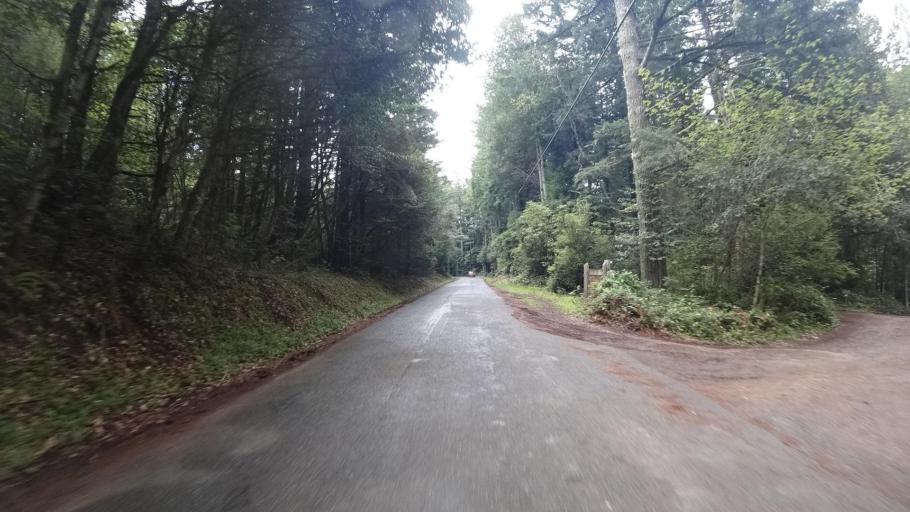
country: US
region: California
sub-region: Humboldt County
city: Blue Lake
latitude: 40.8203
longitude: -123.9985
